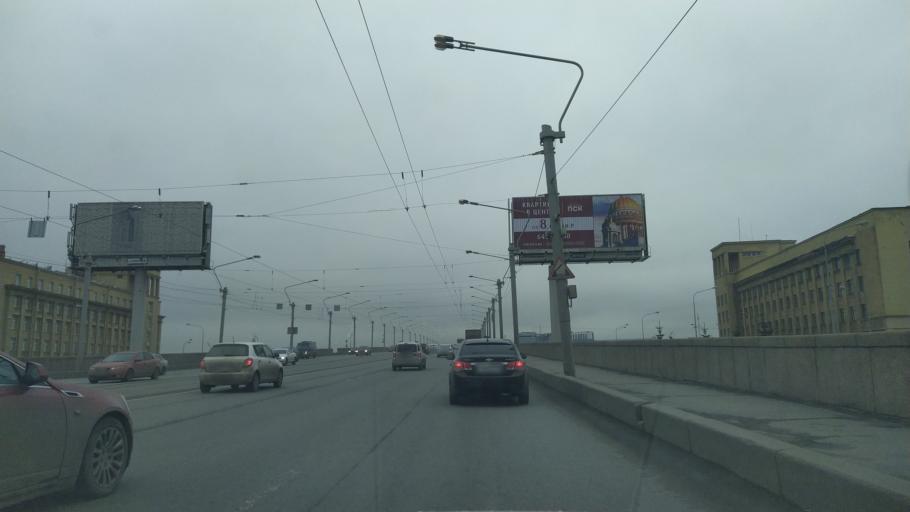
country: RU
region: St.-Petersburg
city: Centralniy
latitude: 59.9275
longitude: 30.4038
